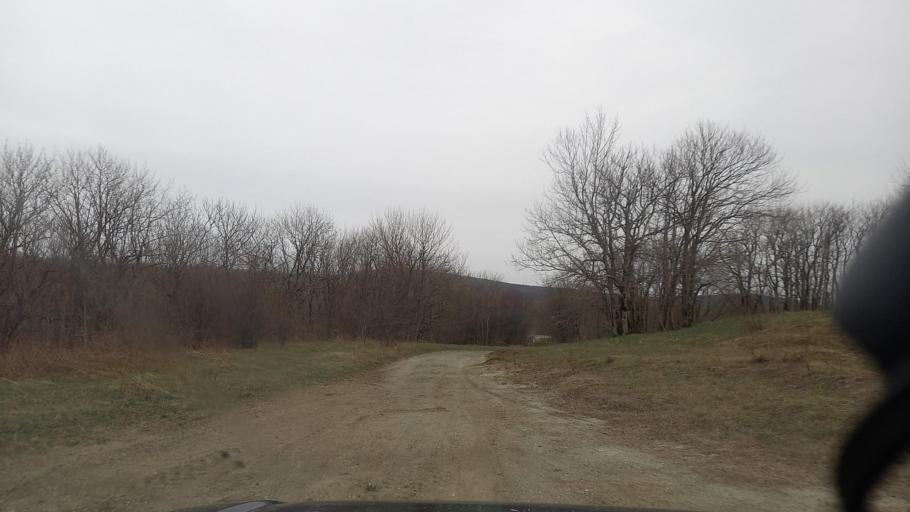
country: RU
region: Krasnodarskiy
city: Divnomorskoye
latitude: 44.6083
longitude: 38.2477
